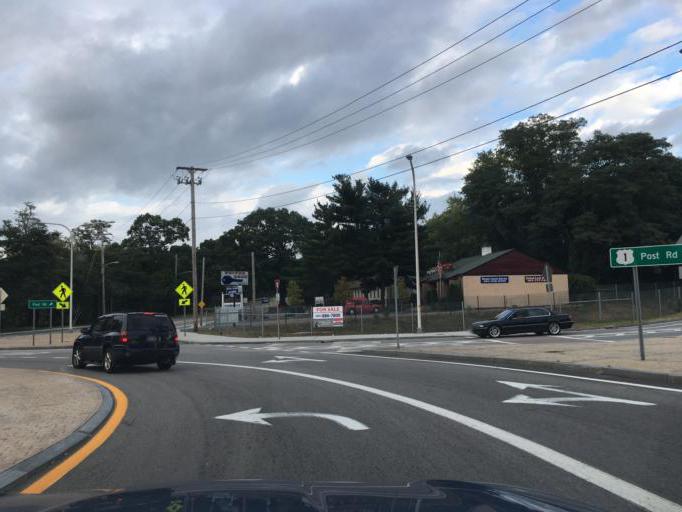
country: US
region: Rhode Island
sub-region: Kent County
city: Warwick
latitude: 41.7024
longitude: -71.4545
